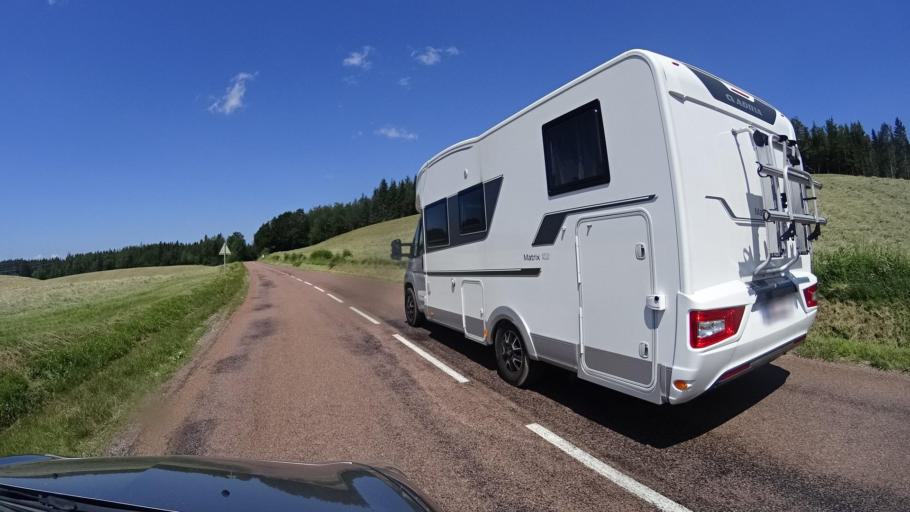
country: FR
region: Franche-Comte
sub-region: Departement du Jura
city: Longchaumois
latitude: 46.5089
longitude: 5.9002
